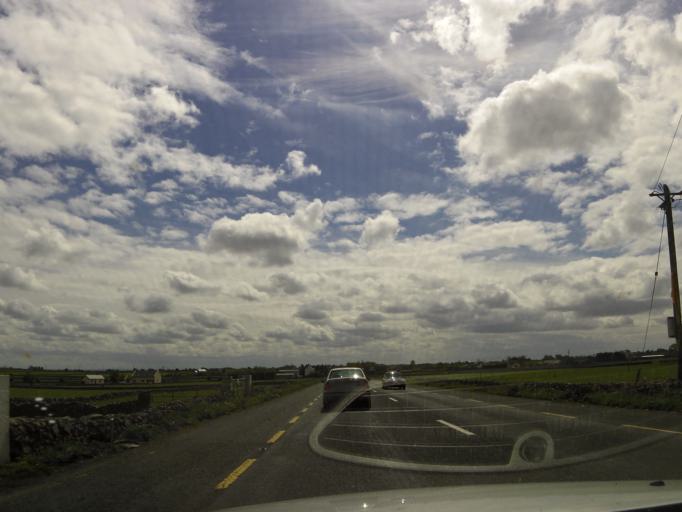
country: IE
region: Connaught
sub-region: County Galway
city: Tuam
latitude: 53.4694
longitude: -8.9093
